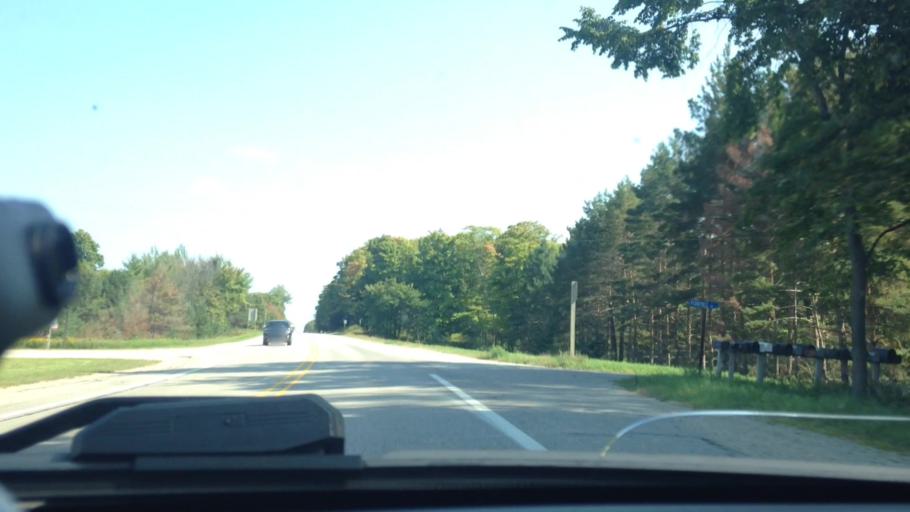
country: US
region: Michigan
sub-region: Luce County
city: Newberry
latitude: 46.3102
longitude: -85.6547
